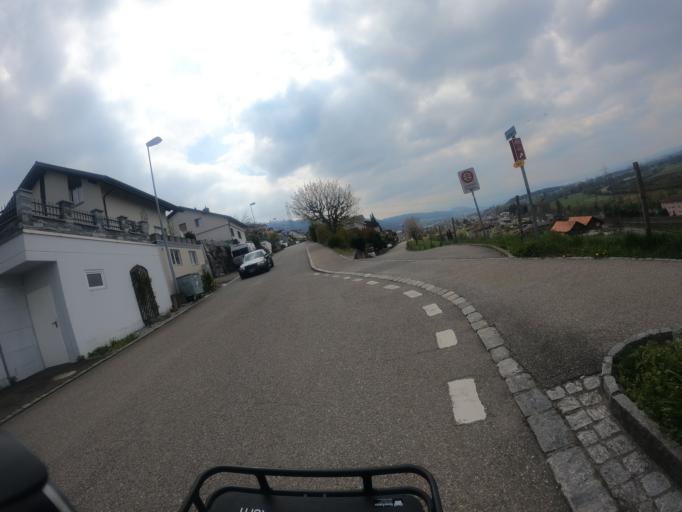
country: CH
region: Lucerne
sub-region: Lucerne-Land District
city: Root
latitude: 47.1242
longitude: 8.3993
